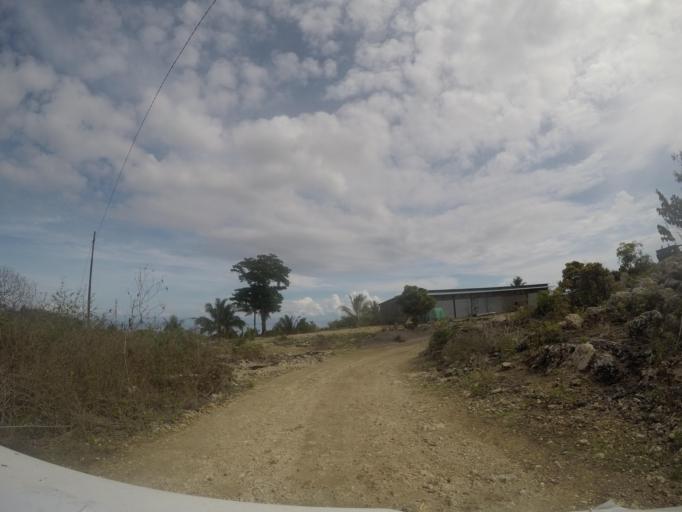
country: TL
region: Baucau
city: Baucau
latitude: -8.4684
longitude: 126.4574
